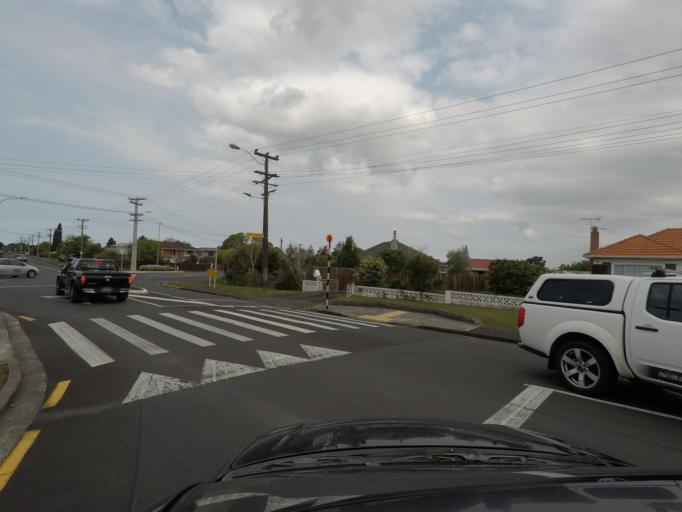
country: NZ
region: Auckland
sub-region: Auckland
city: Rosebank
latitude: -36.8316
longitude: 174.6464
